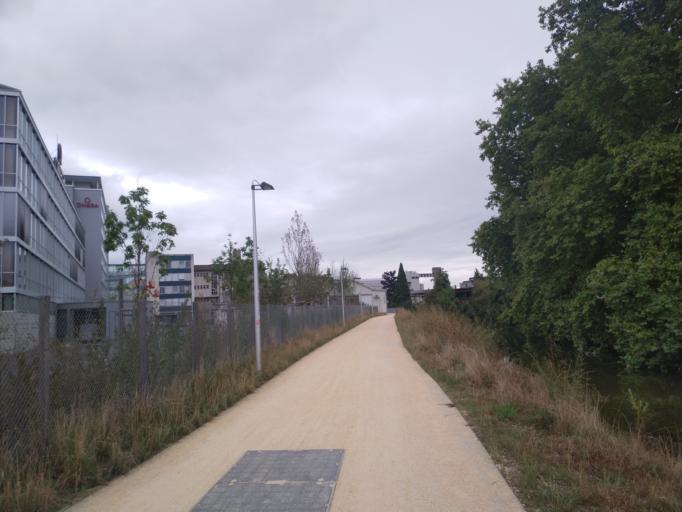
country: CH
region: Bern
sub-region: Biel/Bienne District
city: Biel/Bienne
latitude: 47.1424
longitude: 7.2585
